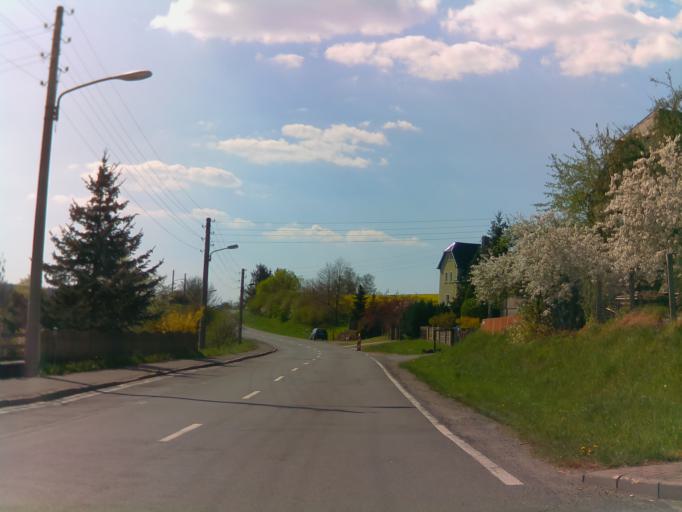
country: DE
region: Saxony
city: Pausa
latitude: 50.6249
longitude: 12.0347
